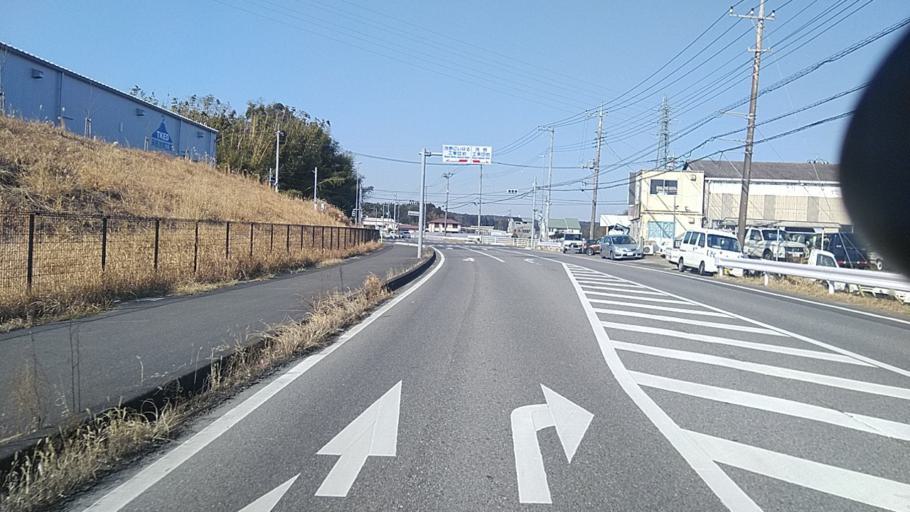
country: JP
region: Chiba
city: Mobara
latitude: 35.4705
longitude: 140.2823
